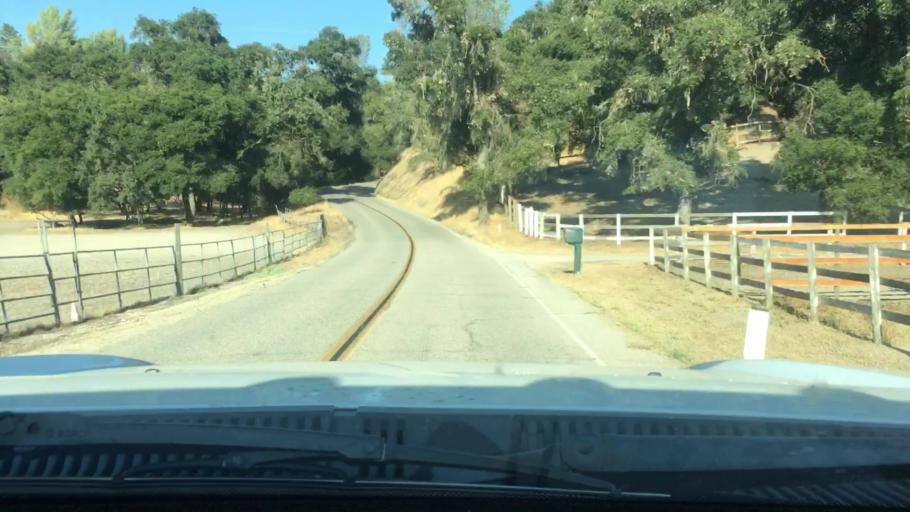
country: US
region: California
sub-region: San Luis Obispo County
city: Atascadero
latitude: 35.4583
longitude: -120.6596
